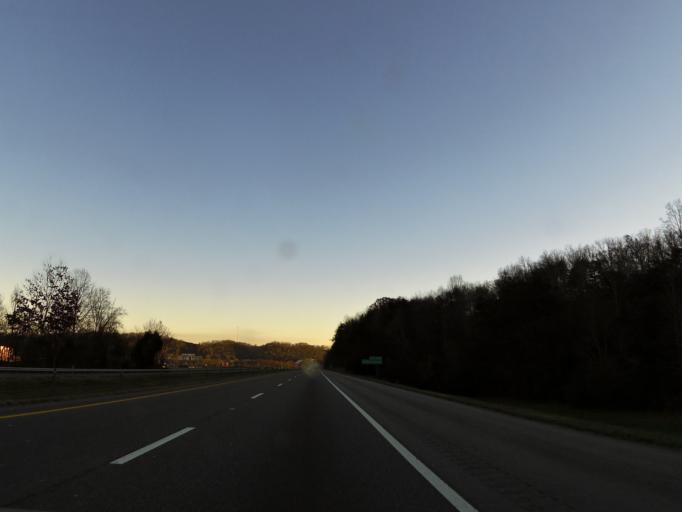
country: US
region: Tennessee
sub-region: Knox County
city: Knoxville
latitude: 36.0578
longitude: -84.0060
